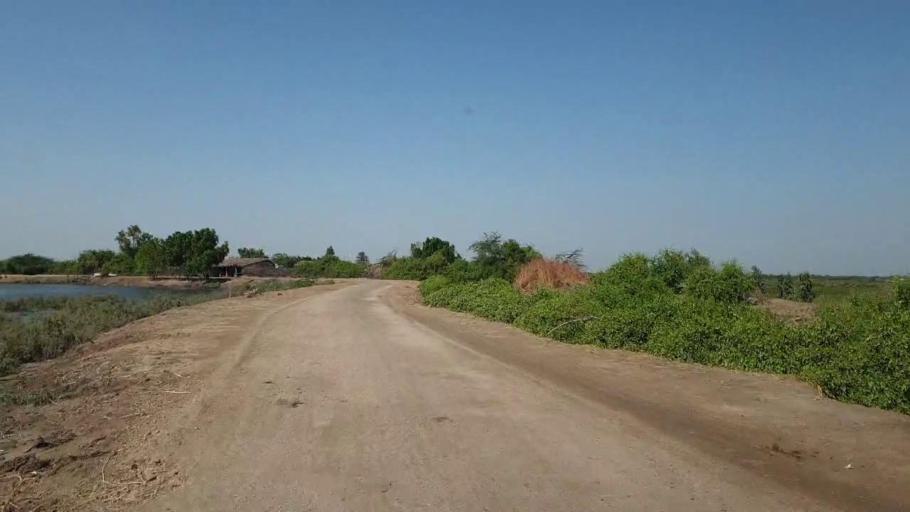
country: PK
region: Sindh
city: Tando Bago
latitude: 24.7055
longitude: 69.0162
